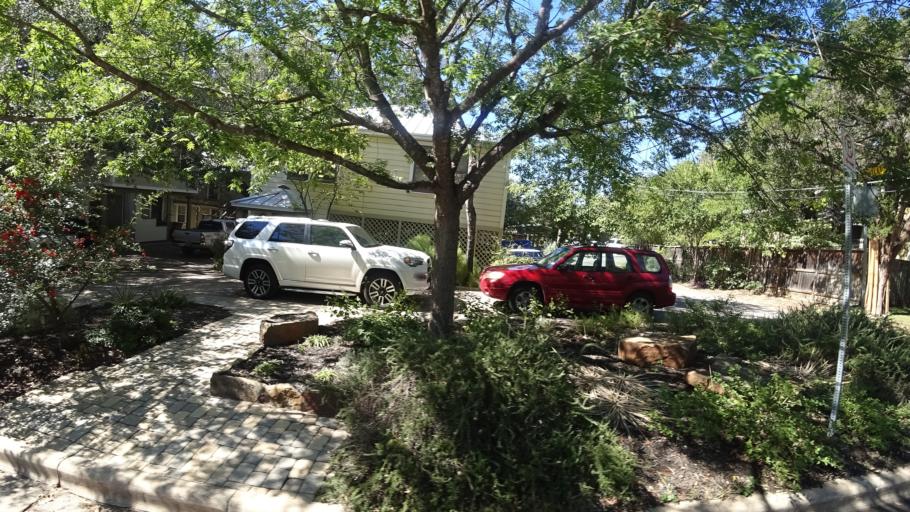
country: US
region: Texas
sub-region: Travis County
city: Rollingwood
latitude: 30.2773
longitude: -97.7661
